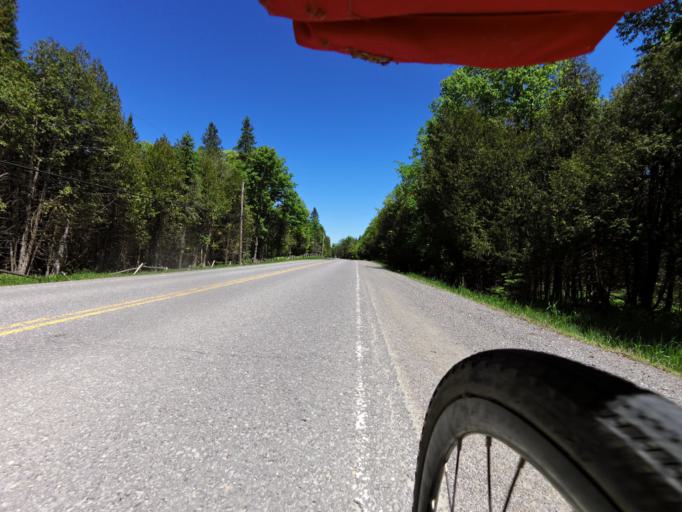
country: CA
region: Ontario
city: Carleton Place
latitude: 45.1812
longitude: -76.3991
